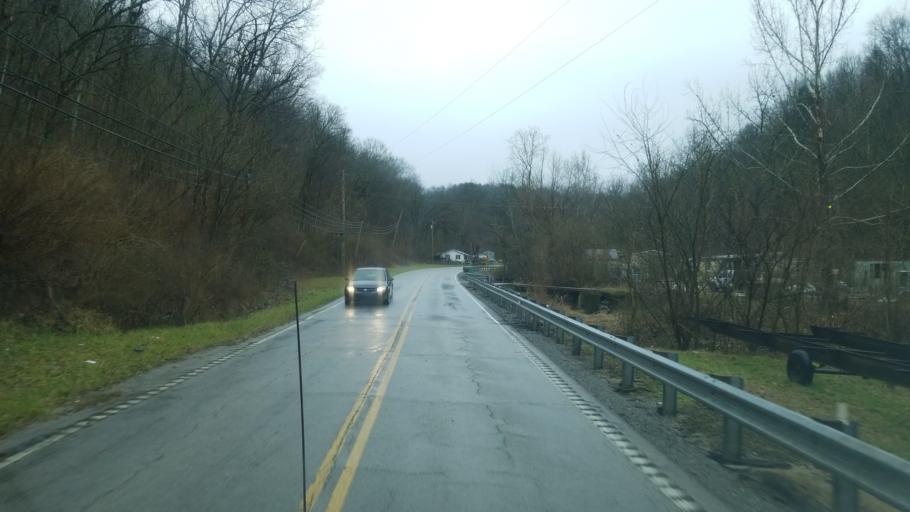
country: US
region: Kentucky
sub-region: Mason County
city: Maysville
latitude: 38.6203
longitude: -83.7008
